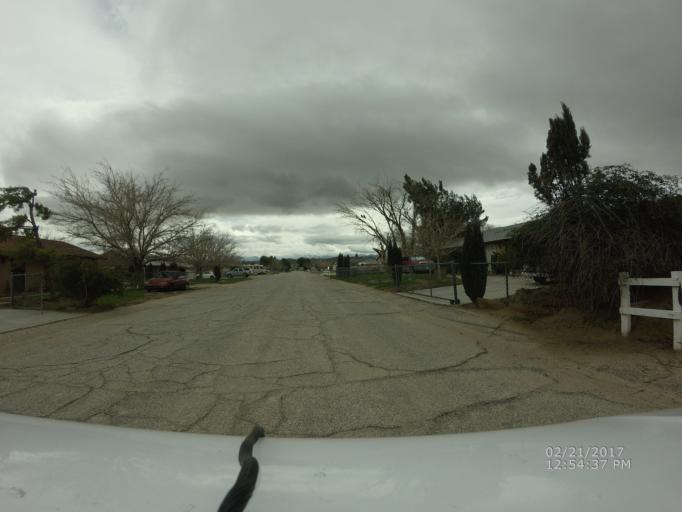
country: US
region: California
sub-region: Los Angeles County
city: Lake Los Angeles
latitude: 34.6418
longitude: -117.8524
